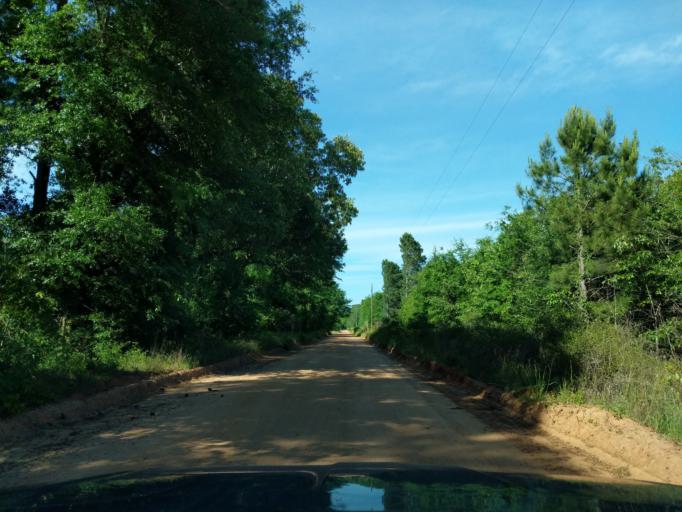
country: US
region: Georgia
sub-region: Jefferson County
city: Wrens
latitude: 33.2223
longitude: -82.3537
